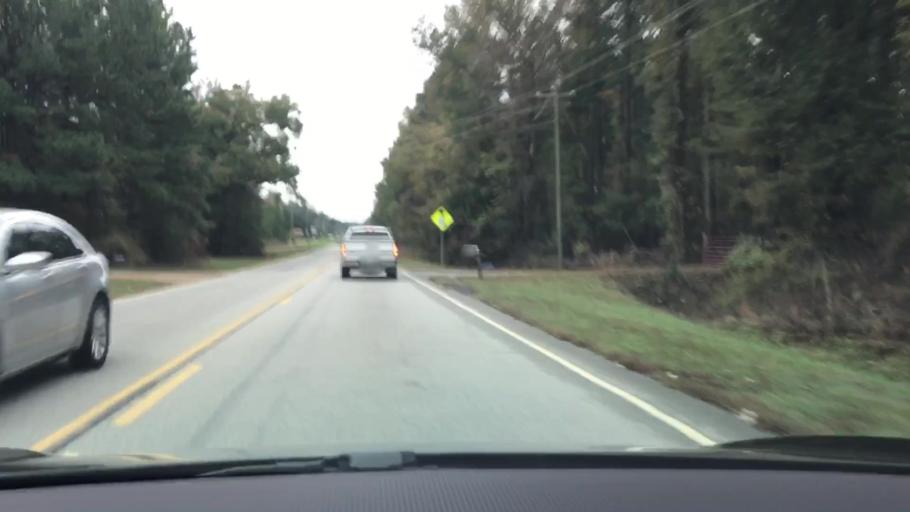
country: US
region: Georgia
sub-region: Warren County
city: West Warrenton
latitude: 33.4218
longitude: -82.6807
